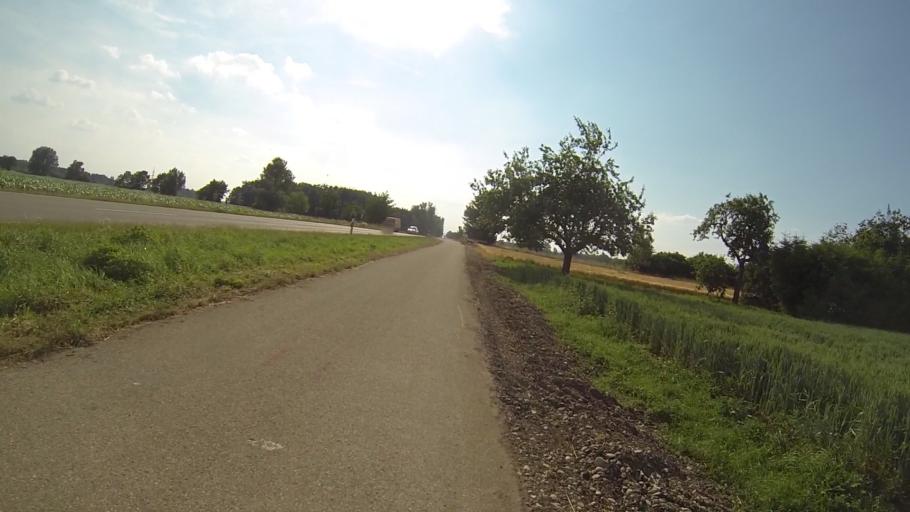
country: DE
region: Bavaria
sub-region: Swabia
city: Holzheim
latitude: 48.3867
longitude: 10.0699
